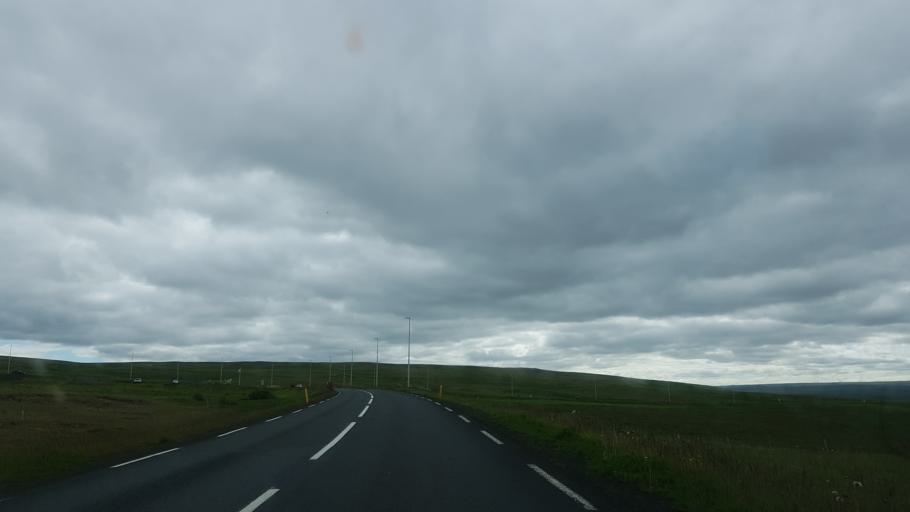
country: IS
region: Northwest
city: Saudarkrokur
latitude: 65.3548
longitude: -20.8879
